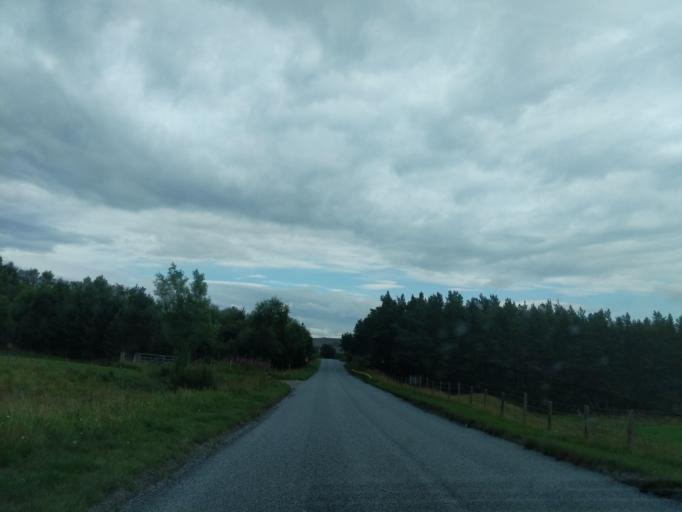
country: GB
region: Scotland
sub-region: Highland
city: Grantown on Spey
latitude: 57.3061
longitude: -3.7407
